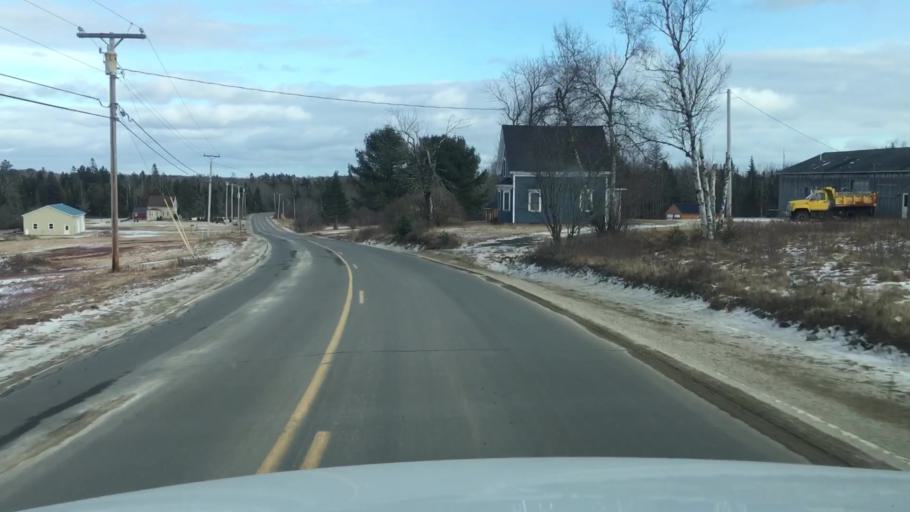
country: US
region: Maine
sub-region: Washington County
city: Jonesport
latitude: 44.6082
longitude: -67.5966
